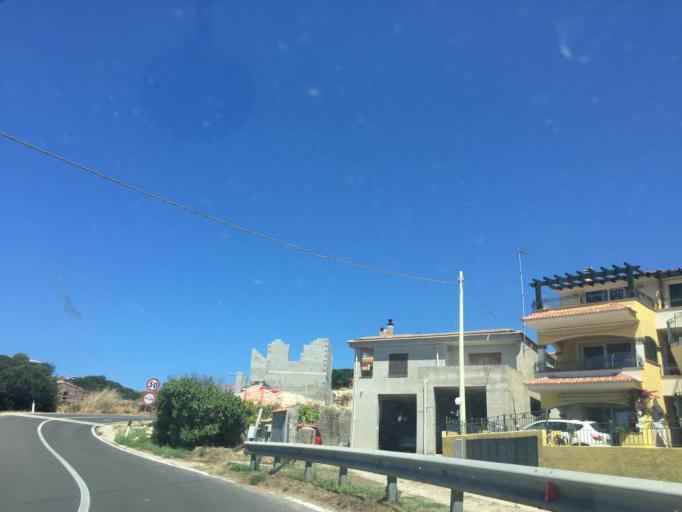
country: IT
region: Sardinia
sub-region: Provincia di Sassari
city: Castelsardo
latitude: 40.9106
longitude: 8.7334
